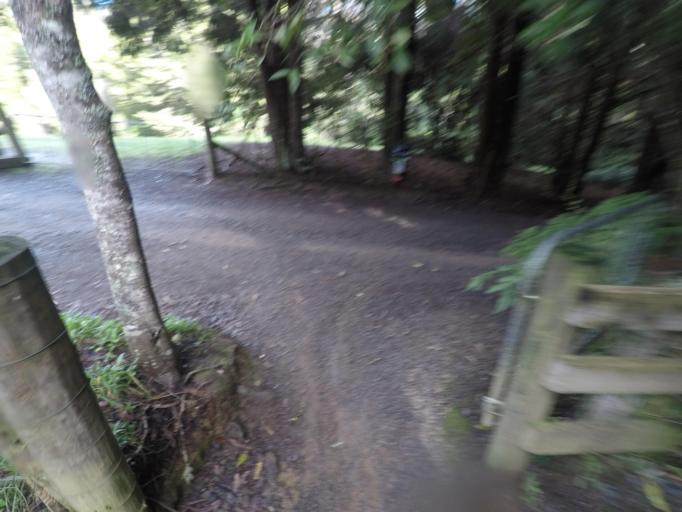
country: NZ
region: Auckland
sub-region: Auckland
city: Manukau City
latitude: -37.0003
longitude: 174.9121
